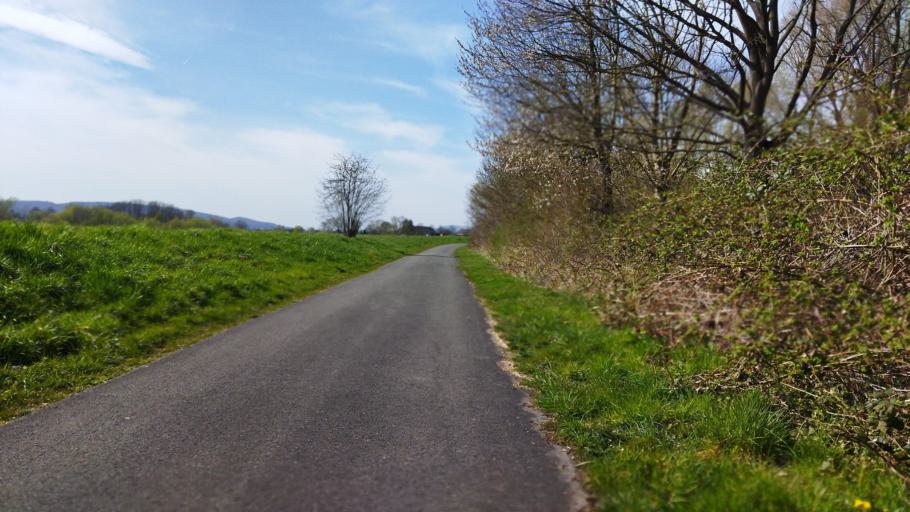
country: DE
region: Lower Saxony
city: Hessisch Oldendorf
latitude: 52.1464
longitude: 9.2748
